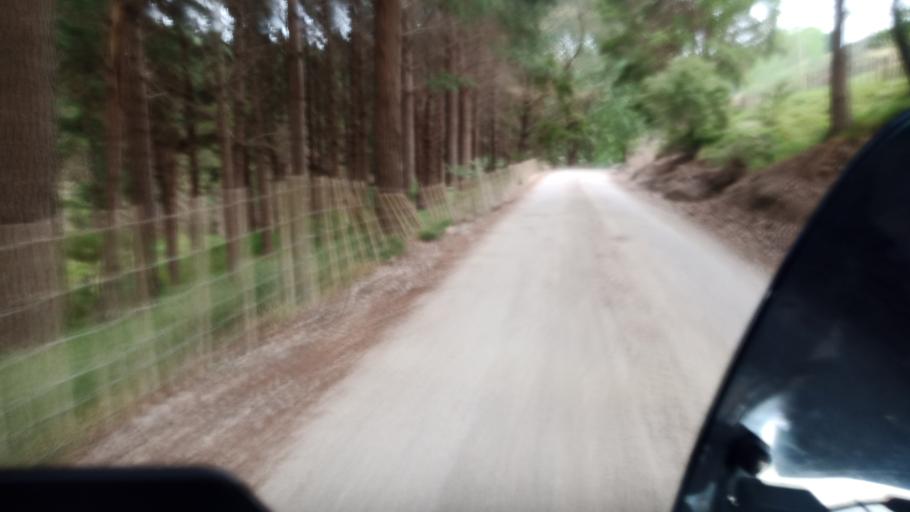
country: NZ
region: Gisborne
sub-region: Gisborne District
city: Gisborne
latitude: -38.4813
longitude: 177.9622
